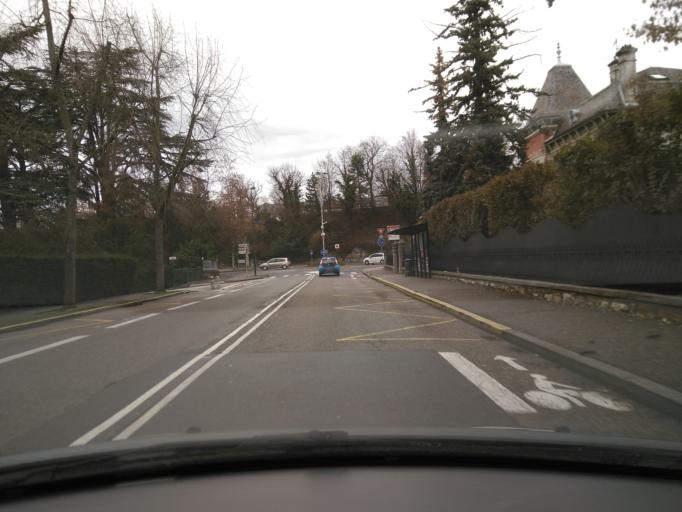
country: FR
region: Rhone-Alpes
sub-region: Departement de la Haute-Savoie
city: Saint-Julien-en-Genevois
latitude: 46.1430
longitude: 6.0852
